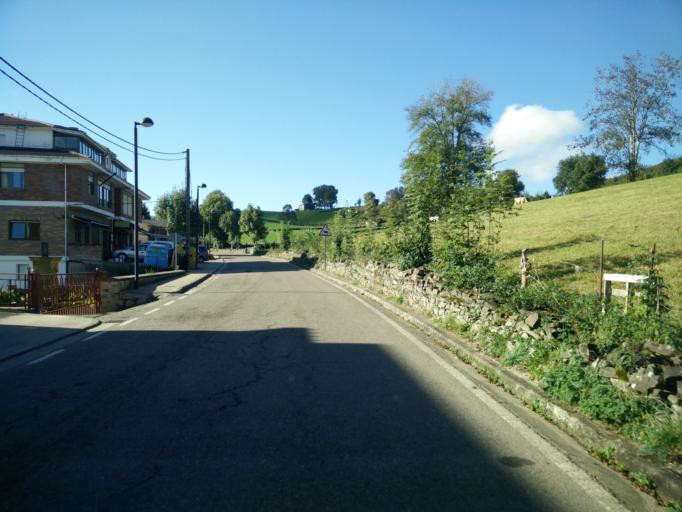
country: ES
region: Cantabria
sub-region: Provincia de Cantabria
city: San Pedro del Romeral
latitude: 43.1138
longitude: -3.8187
